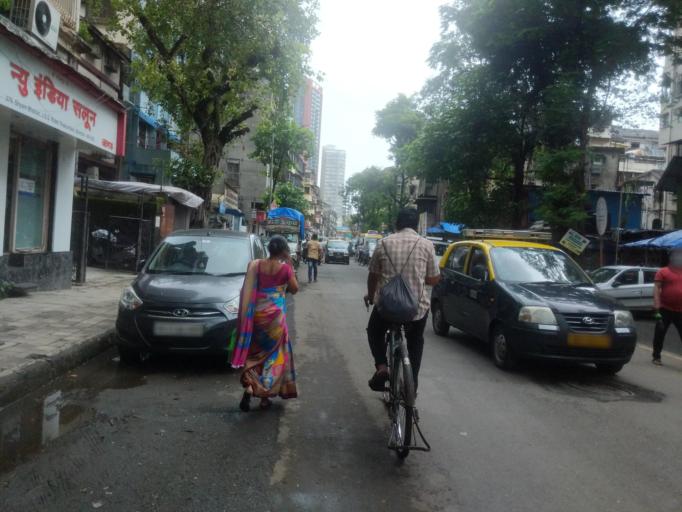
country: IN
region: Maharashtra
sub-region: Raigarh
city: Uran
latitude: 18.9500
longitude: 72.8245
